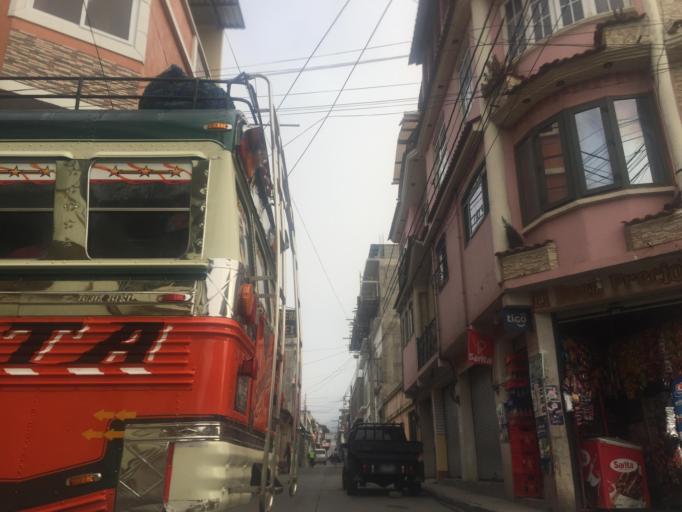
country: GT
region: Totonicapan
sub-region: Municipio de Totonicapan
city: Totonicapan
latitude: 14.9093
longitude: -91.3599
